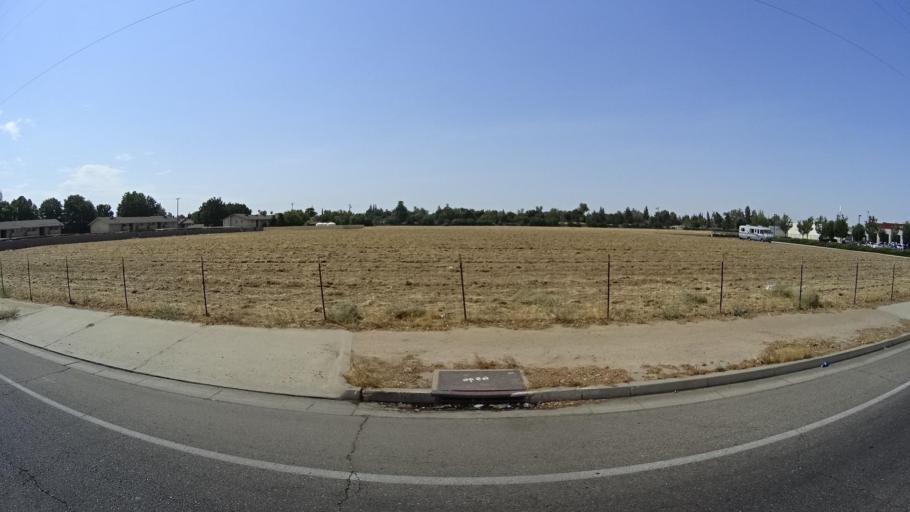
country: US
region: California
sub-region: Fresno County
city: Sunnyside
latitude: 36.7363
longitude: -119.6935
